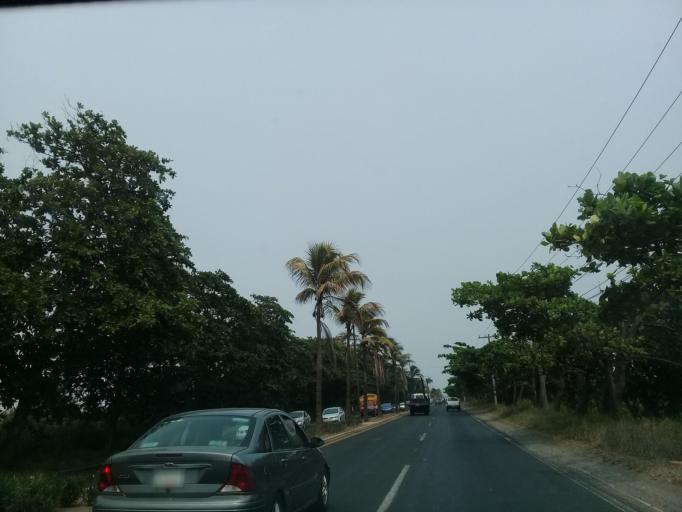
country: MX
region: Veracruz
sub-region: Veracruz
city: Hacienda Sotavento
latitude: 19.1466
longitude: -96.1662
